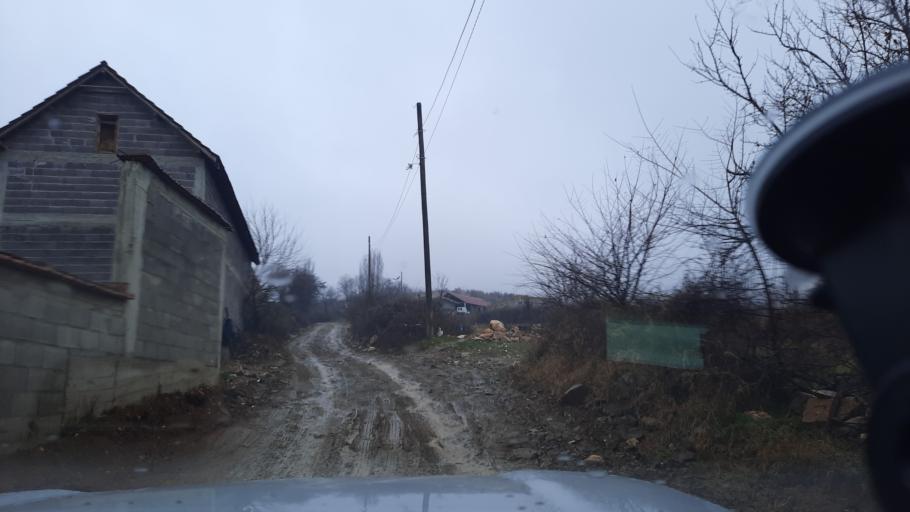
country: MK
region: Opstina Lipkovo
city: Matejche
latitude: 42.1250
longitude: 21.5882
